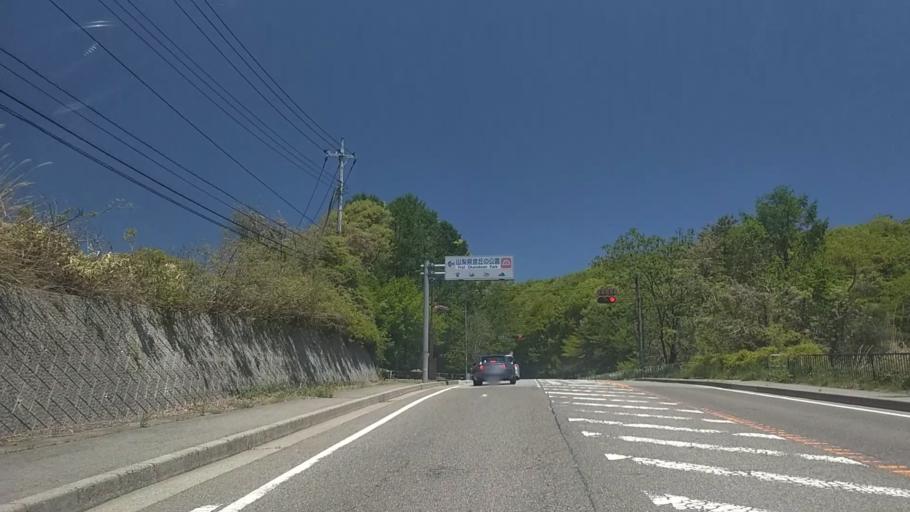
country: JP
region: Yamanashi
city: Nirasaki
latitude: 35.8929
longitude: 138.4405
